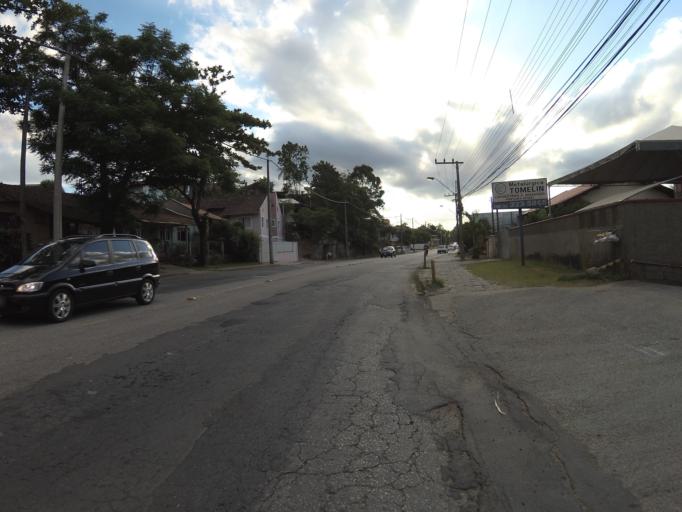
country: BR
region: Santa Catarina
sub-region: Blumenau
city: Blumenau
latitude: -26.8841
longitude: -49.1086
